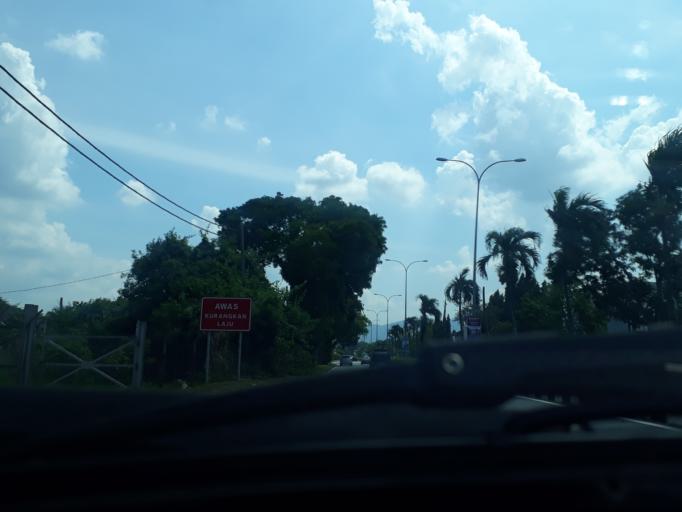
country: MY
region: Perak
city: Ipoh
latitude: 4.5775
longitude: 101.0998
